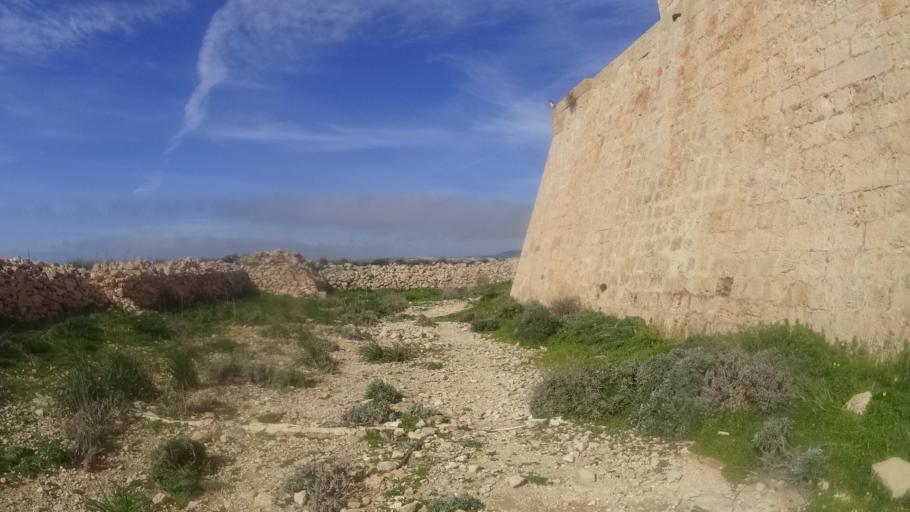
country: MT
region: Il-Qala
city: Qala
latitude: 36.0067
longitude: 14.3297
